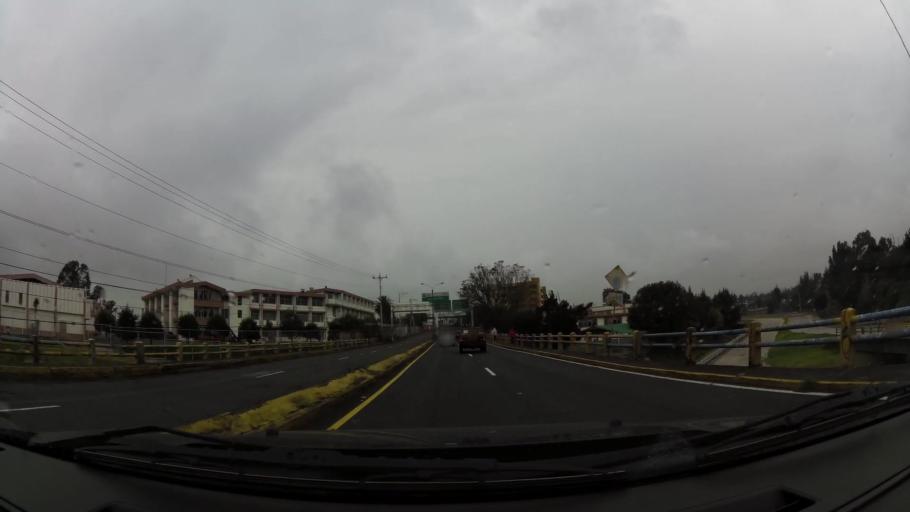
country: EC
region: Pichincha
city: Sangolqui
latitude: -0.2945
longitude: -78.4627
